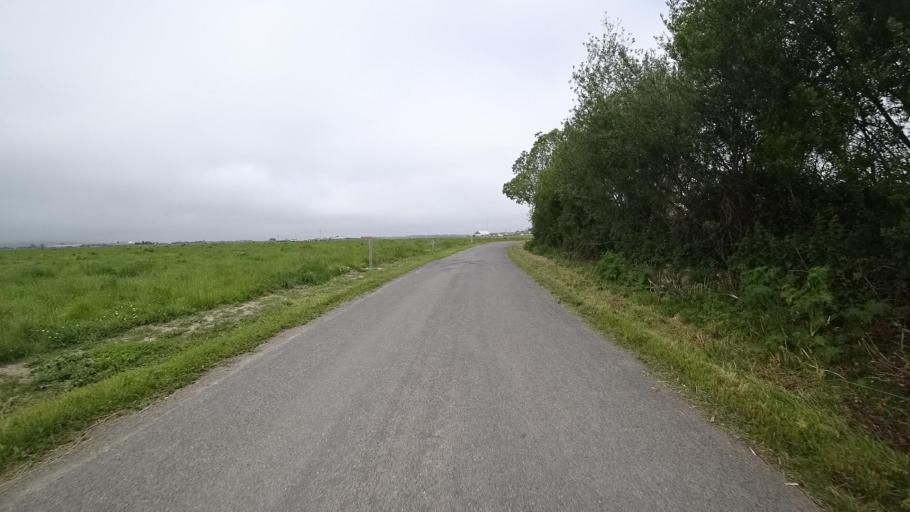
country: US
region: California
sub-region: Humboldt County
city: Fortuna
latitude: 40.5902
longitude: -124.1885
